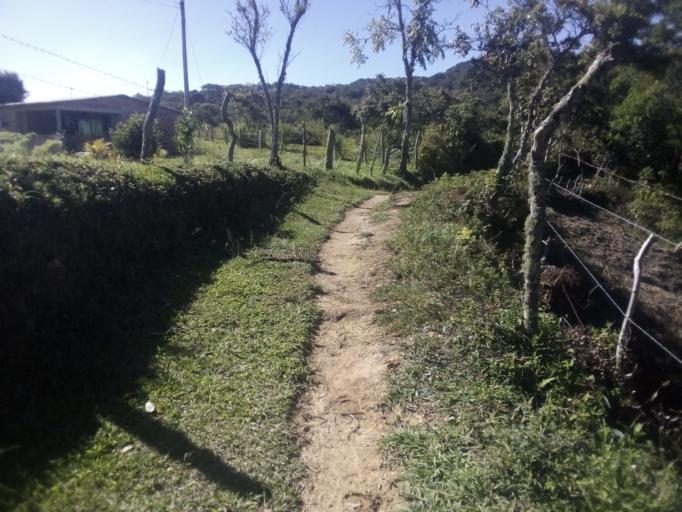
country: CO
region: Santander
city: Guepsa
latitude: 5.9921
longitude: -73.5544
